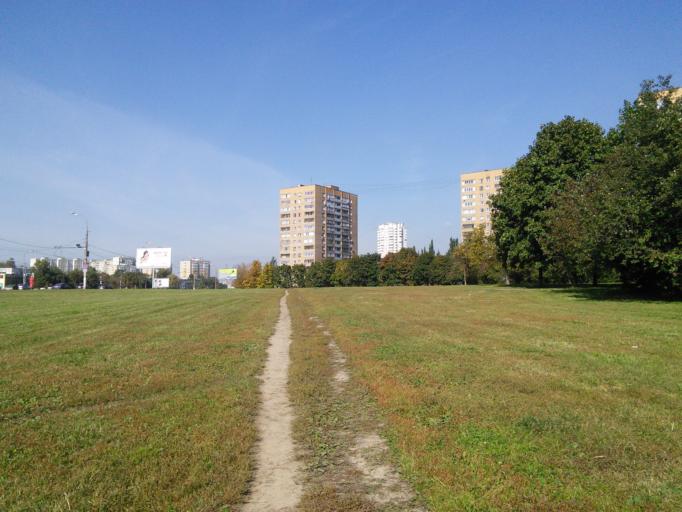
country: RU
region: Moscow
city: Tsaritsyno
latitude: 55.6321
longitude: 37.6611
